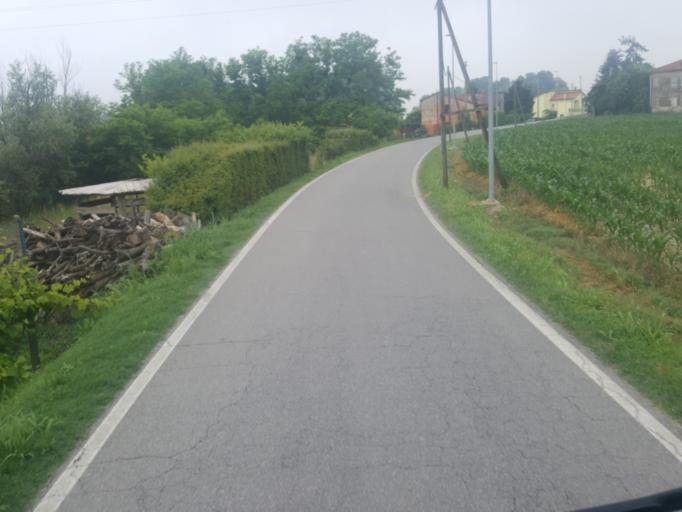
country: IT
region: Veneto
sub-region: Provincia di Rovigo
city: Canaro
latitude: 44.9343
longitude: 11.6645
